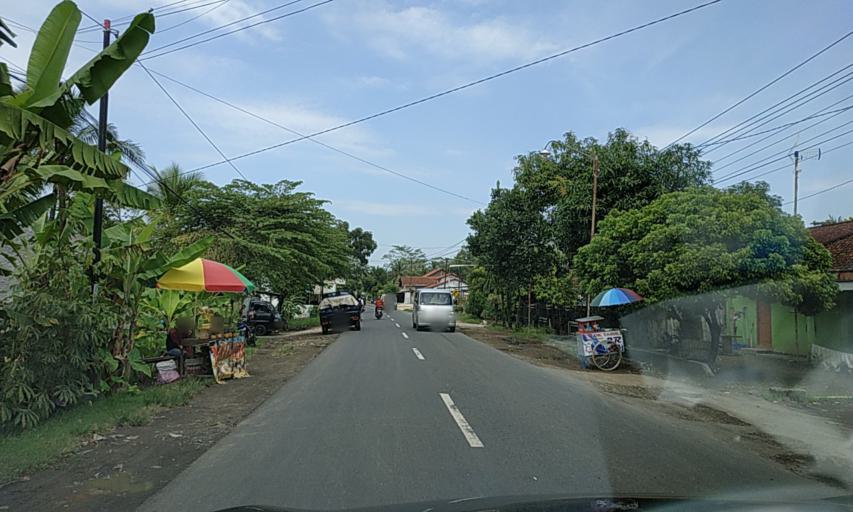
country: ID
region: Central Java
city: Mulyosari
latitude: -7.5028
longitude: 108.7860
